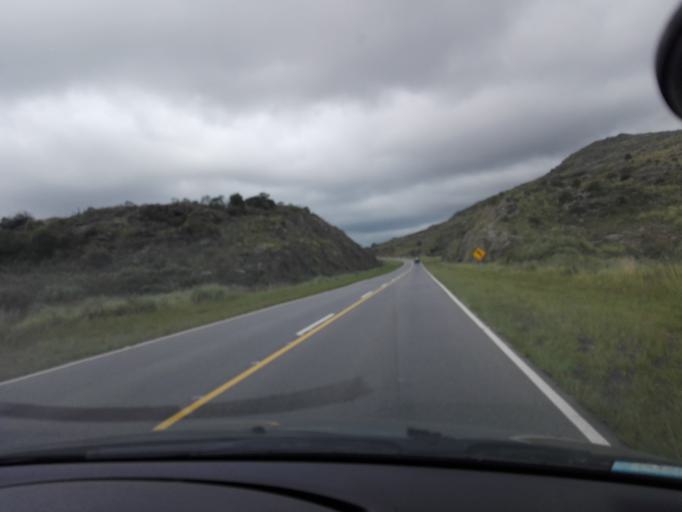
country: AR
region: Cordoba
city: Cuesta Blanca
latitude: -31.5981
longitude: -64.6775
